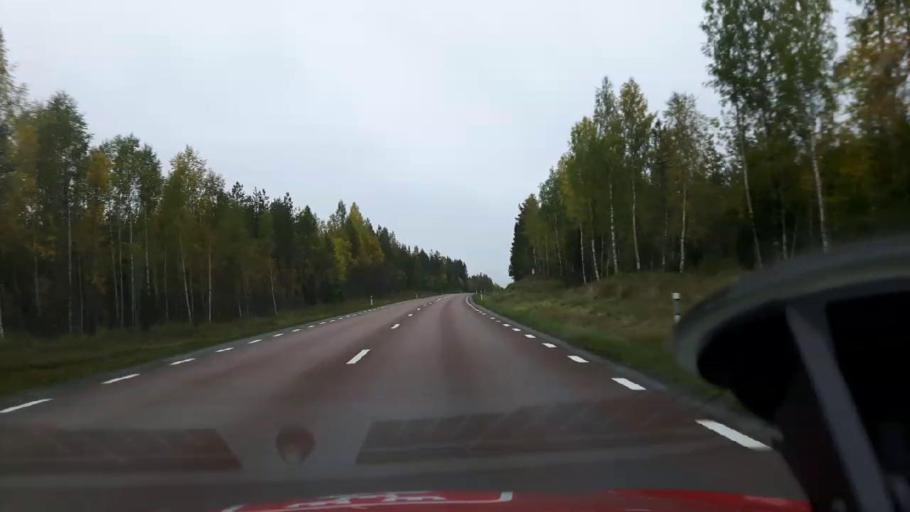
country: SE
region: Jaemtland
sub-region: Bergs Kommun
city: Hoverberg
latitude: 62.8338
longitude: 14.5195
